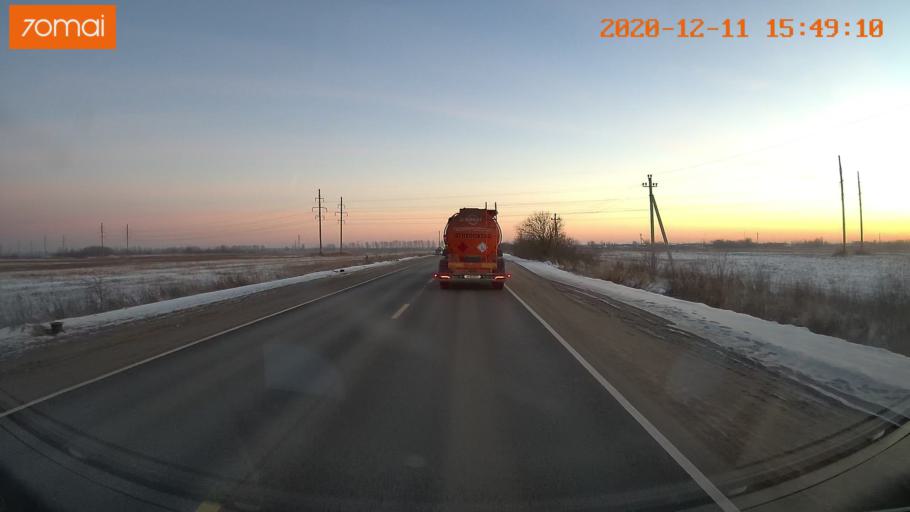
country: RU
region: Ivanovo
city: Novo-Talitsy
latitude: 56.9897
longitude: 40.8725
